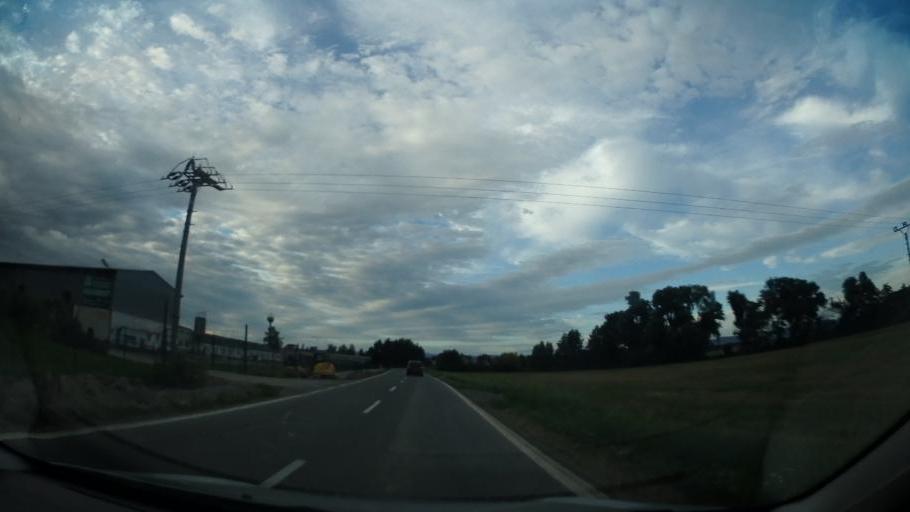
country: CZ
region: Olomoucky
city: Cervenka
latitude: 49.7444
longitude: 17.0884
